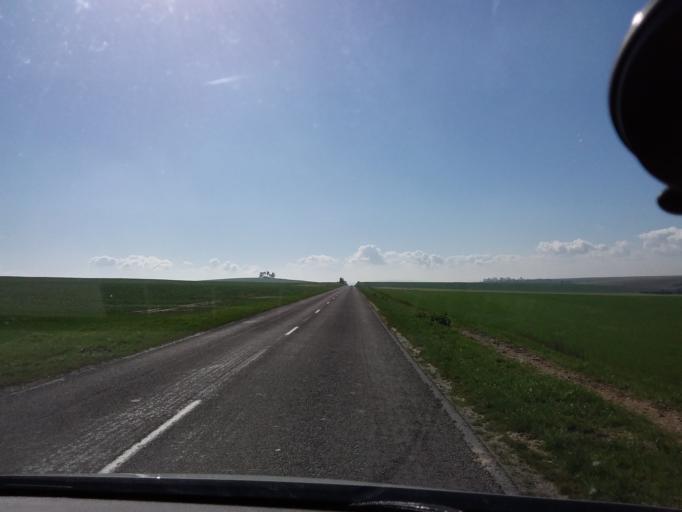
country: FR
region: Picardie
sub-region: Departement de l'Aisne
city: Guignicourt
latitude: 49.4599
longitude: 4.0404
